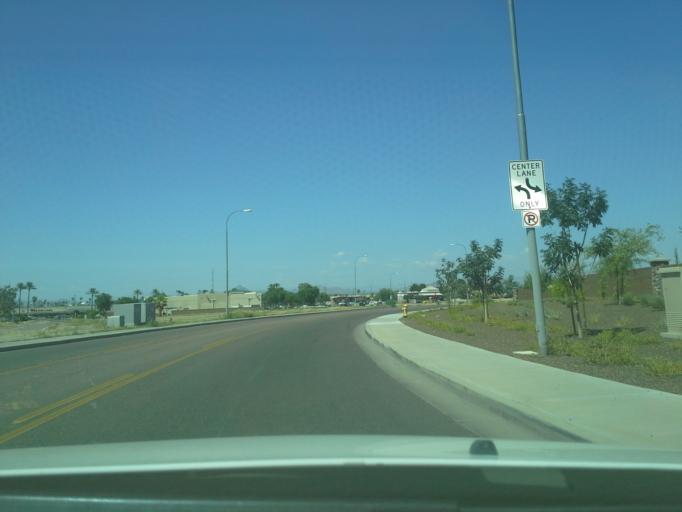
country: US
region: Arizona
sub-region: Maricopa County
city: Phoenix
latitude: 33.3746
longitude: -112.0659
